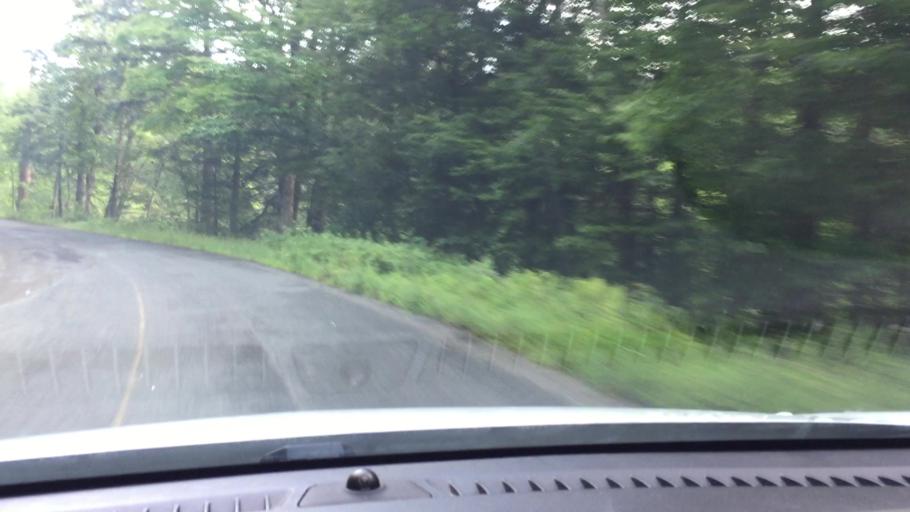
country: US
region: Massachusetts
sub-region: Hampshire County
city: Chesterfield
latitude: 42.3115
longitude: -72.9181
